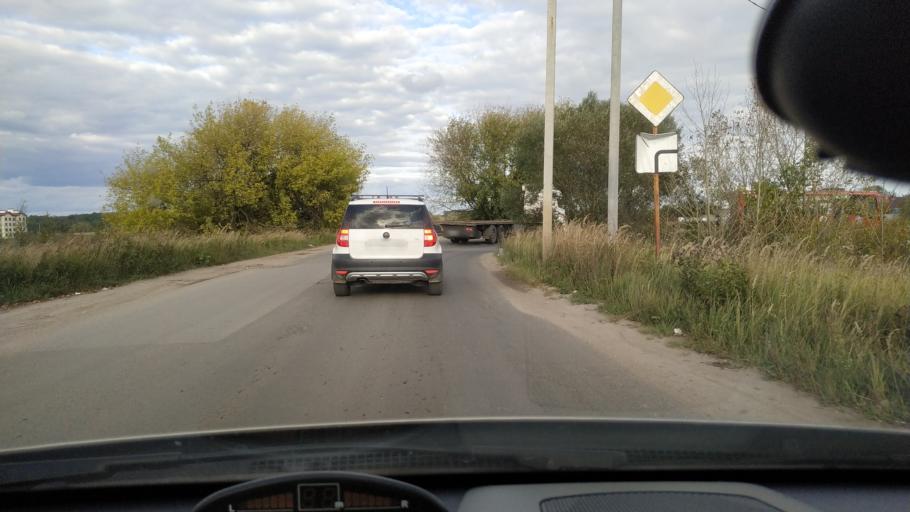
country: RU
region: Rjazan
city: Polyany
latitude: 54.5837
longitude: 39.8386
